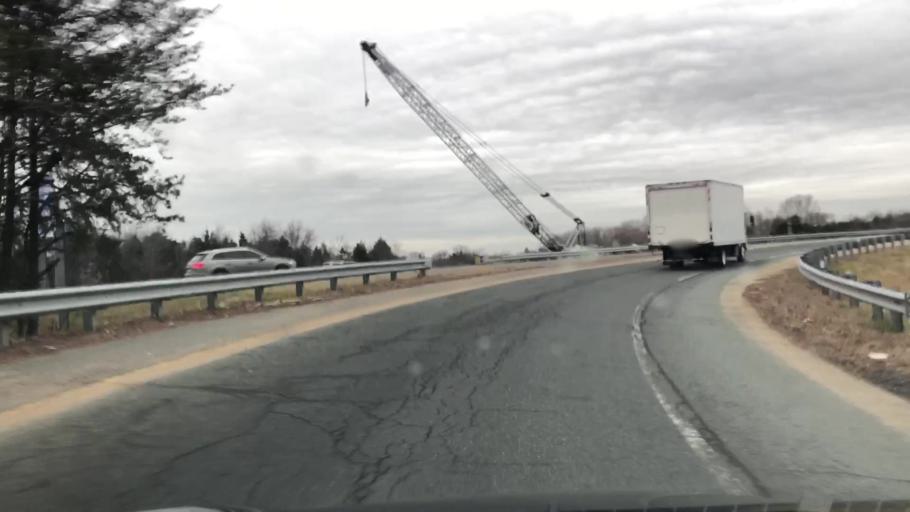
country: US
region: Virginia
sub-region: Stafford County
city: Falmouth
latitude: 38.3389
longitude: -77.4924
